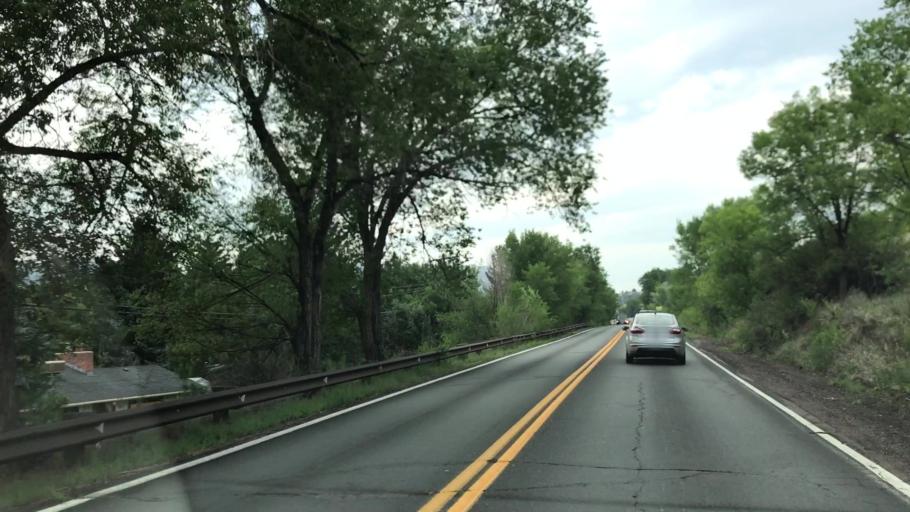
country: US
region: Colorado
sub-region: El Paso County
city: Manitou Springs
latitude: 38.8631
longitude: -104.8662
